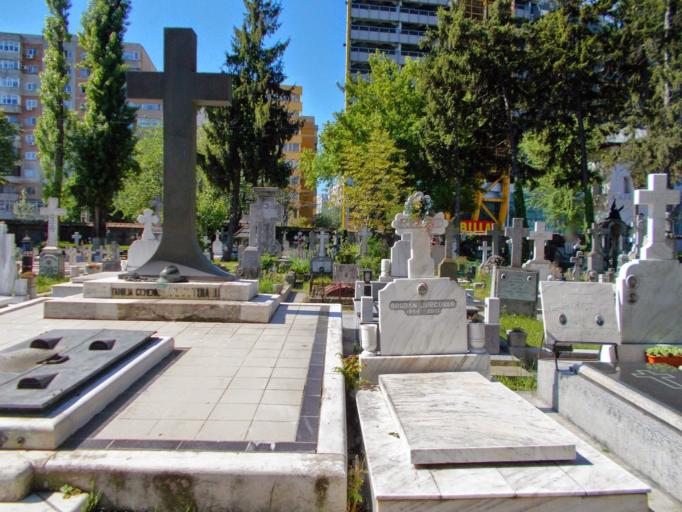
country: RO
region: Bucuresti
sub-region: Municipiul Bucuresti
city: Bucuresti
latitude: 44.4017
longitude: 26.1005
